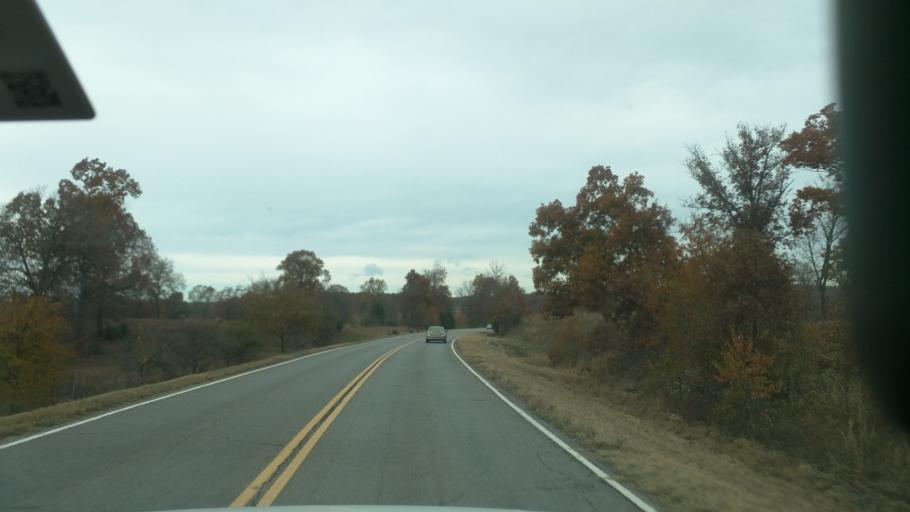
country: US
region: Oklahoma
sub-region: Cherokee County
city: Park Hill
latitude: 35.9039
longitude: -94.8258
